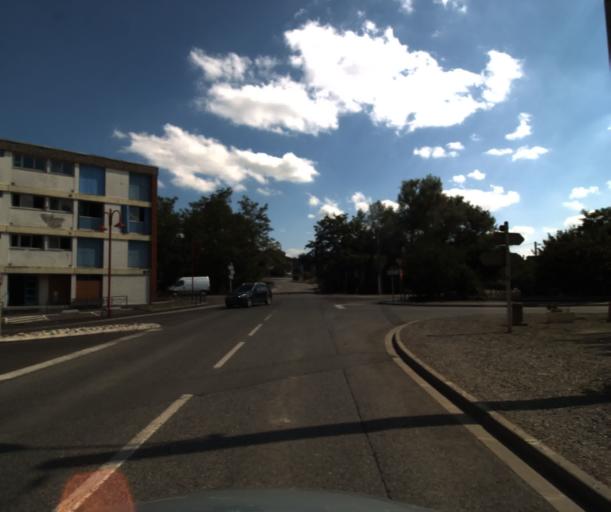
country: FR
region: Midi-Pyrenees
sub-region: Departement de la Haute-Garonne
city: Saint-Lys
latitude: 43.5158
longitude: 1.1752
